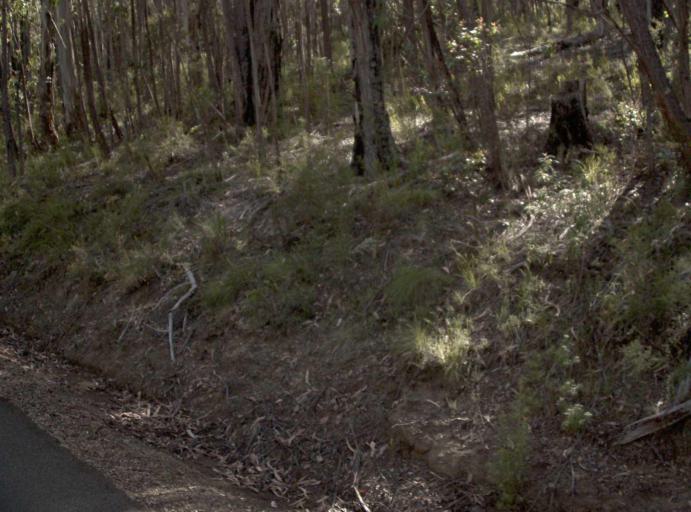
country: AU
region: Victoria
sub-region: East Gippsland
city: Lakes Entrance
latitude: -37.4408
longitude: 148.1316
